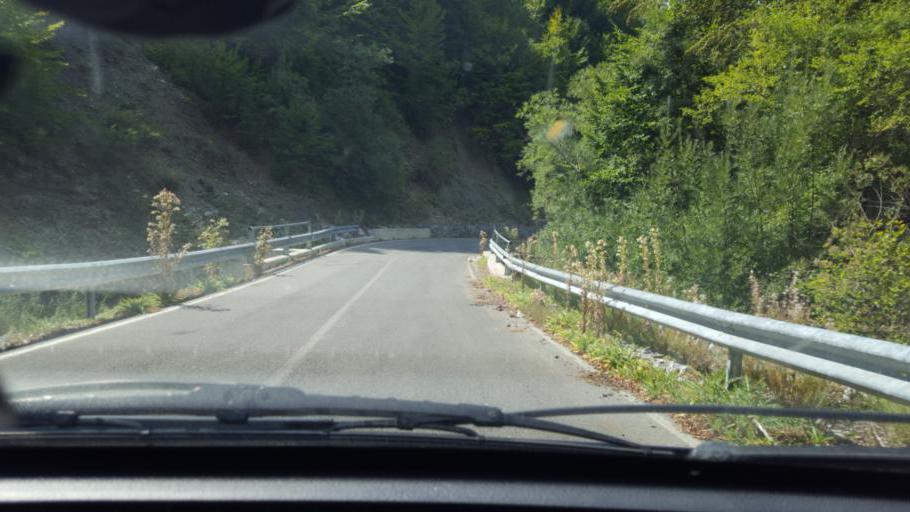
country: AL
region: Kukes
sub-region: Rrethi i Tropojes
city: Valbone
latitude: 42.5370
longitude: 19.6993
